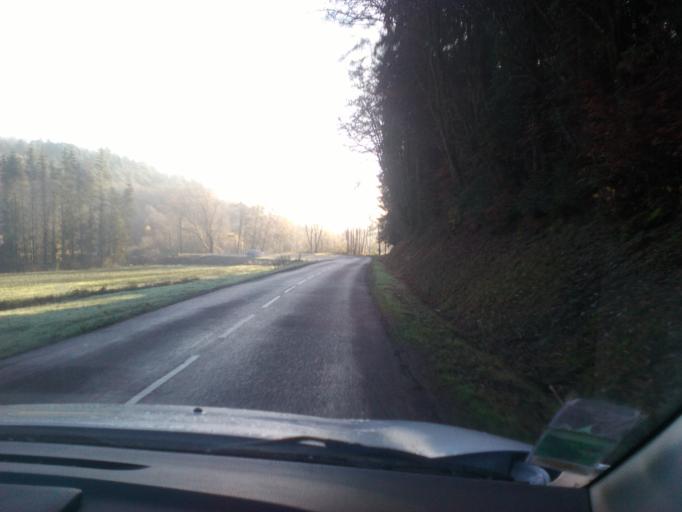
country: FR
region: Lorraine
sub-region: Departement des Vosges
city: Uzemain
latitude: 48.0700
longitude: 6.3124
